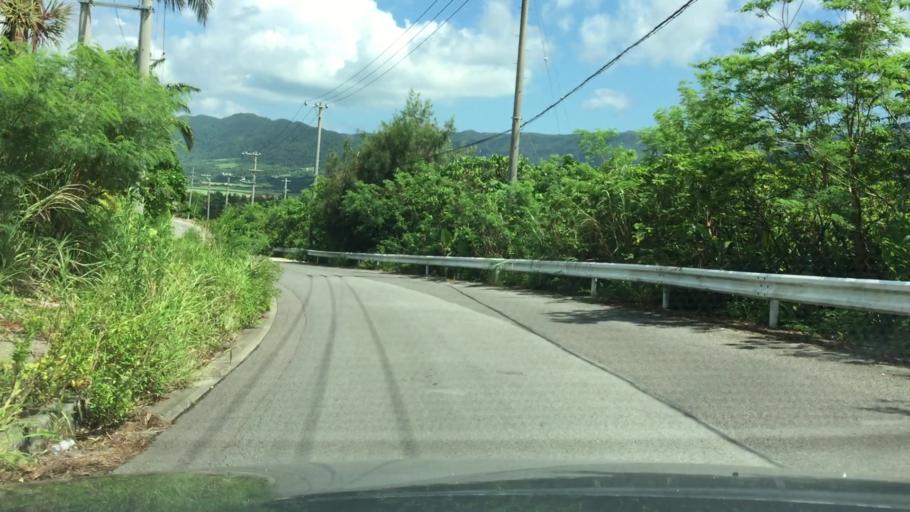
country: JP
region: Okinawa
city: Ishigaki
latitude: 24.3866
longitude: 124.1740
